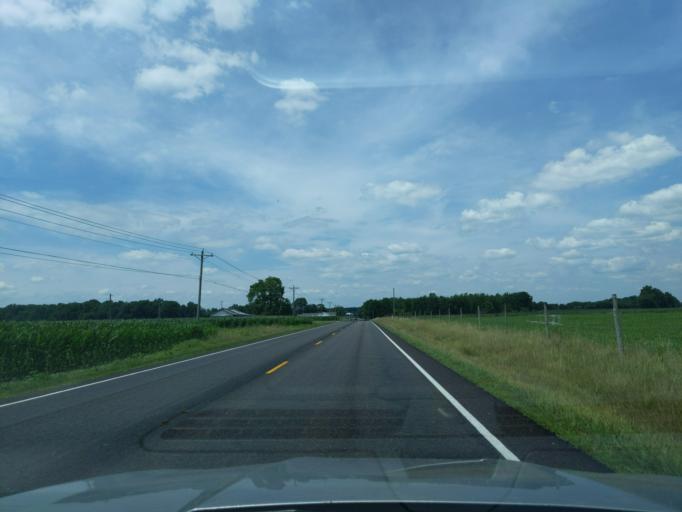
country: US
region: Indiana
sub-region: Ripley County
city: Osgood
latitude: 39.2376
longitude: -85.3433
